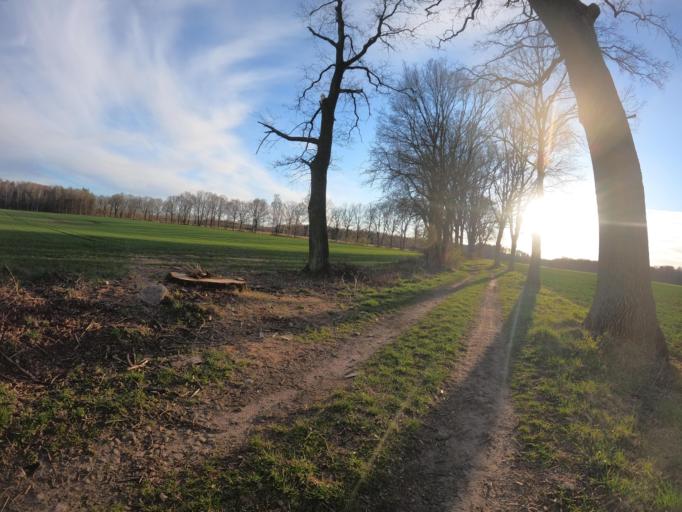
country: PL
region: West Pomeranian Voivodeship
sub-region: Powiat gryficki
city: Gryfice
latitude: 53.8994
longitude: 15.2741
